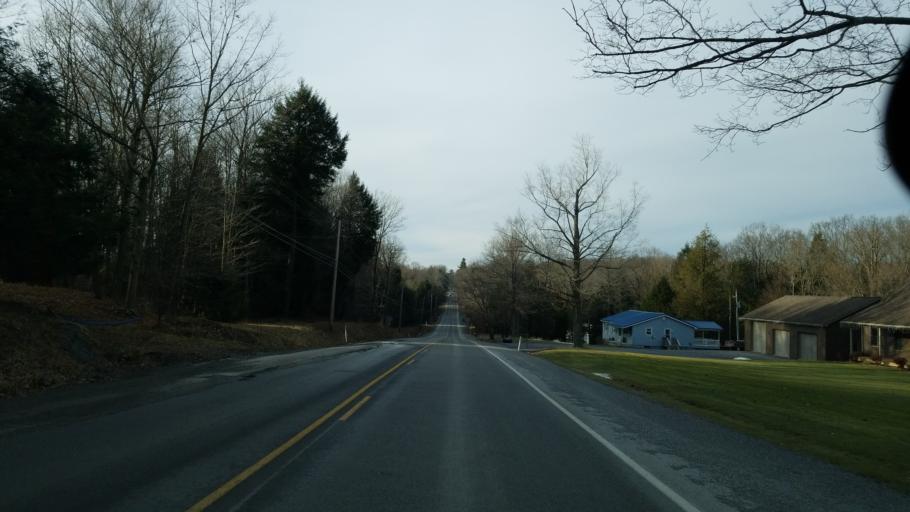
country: US
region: Pennsylvania
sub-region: Clearfield County
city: DuBois
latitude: 41.0251
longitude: -78.6674
